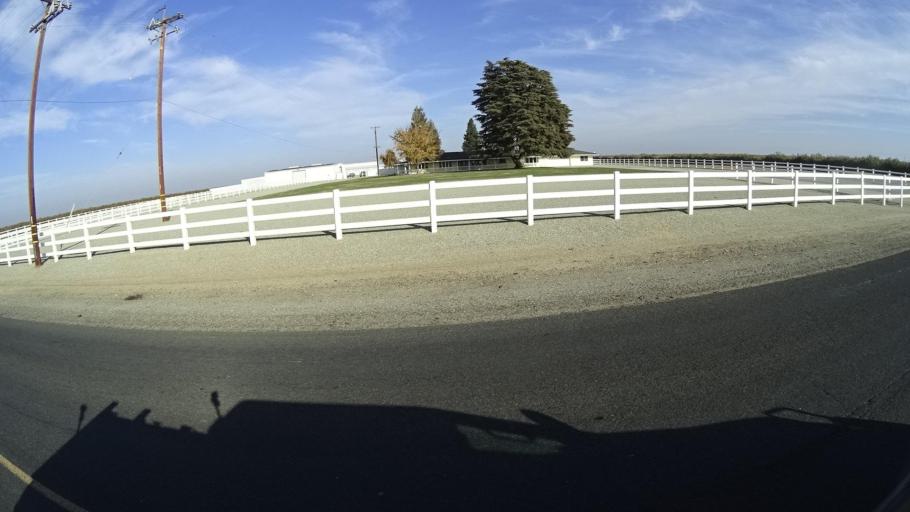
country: US
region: California
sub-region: Kern County
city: McFarland
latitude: 35.6018
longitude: -119.1523
